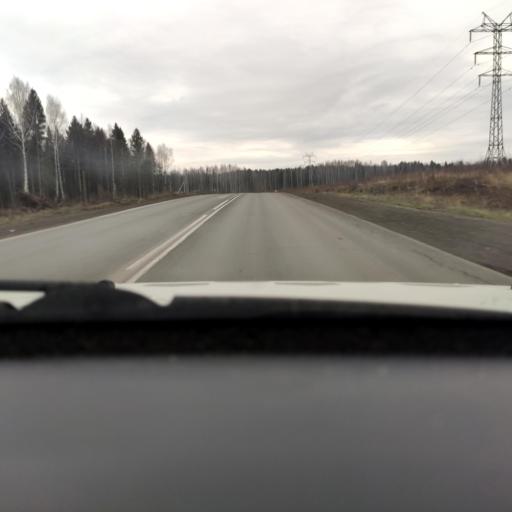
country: RU
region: Perm
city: Polazna
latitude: 58.1359
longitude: 56.4141
